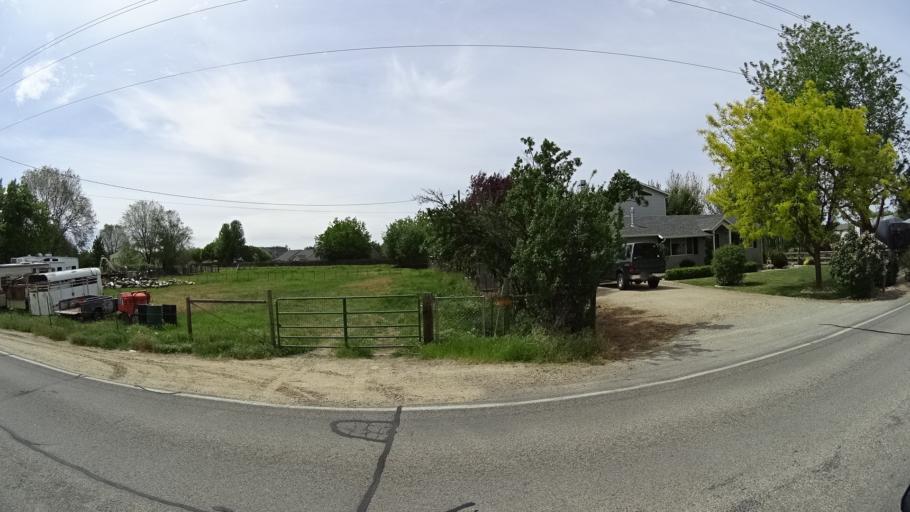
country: US
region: Idaho
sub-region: Ada County
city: Meridian
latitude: 43.5612
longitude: -116.3320
